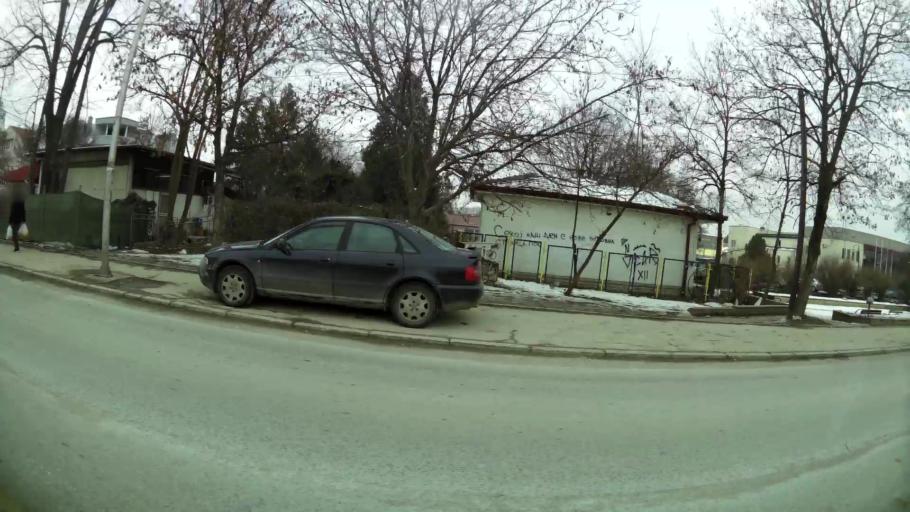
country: MK
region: Butel
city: Butel
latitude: 42.0320
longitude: 21.4453
